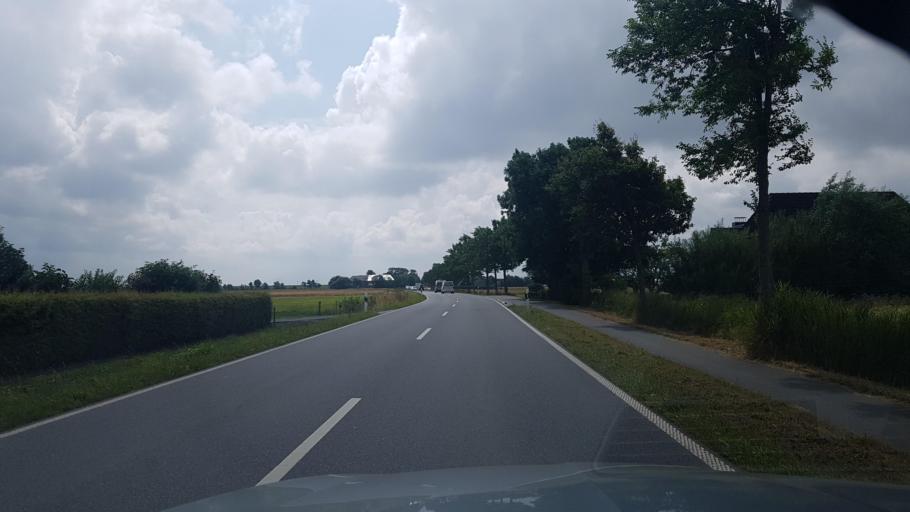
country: DE
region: Schleswig-Holstein
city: Elisabeth-Sophien-Koog
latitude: 54.5051
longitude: 8.9375
